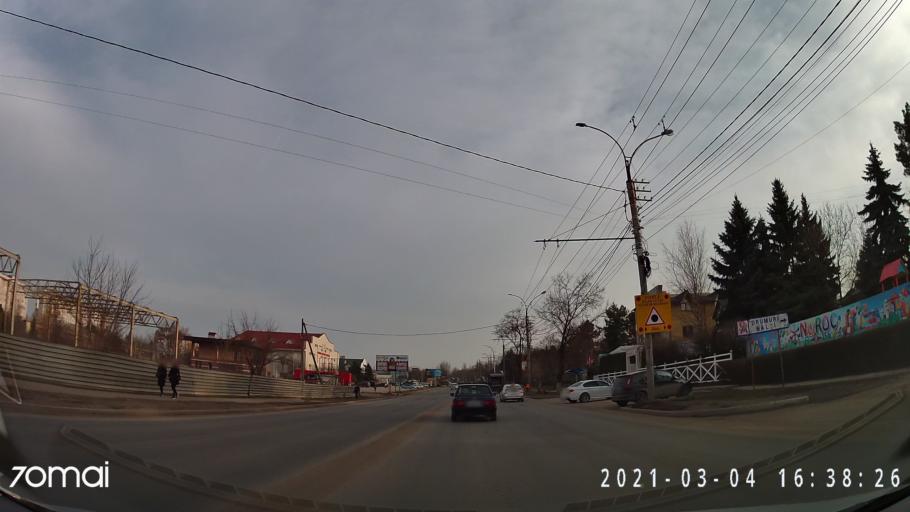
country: MD
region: Balti
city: Balti
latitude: 47.7810
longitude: 27.8909
